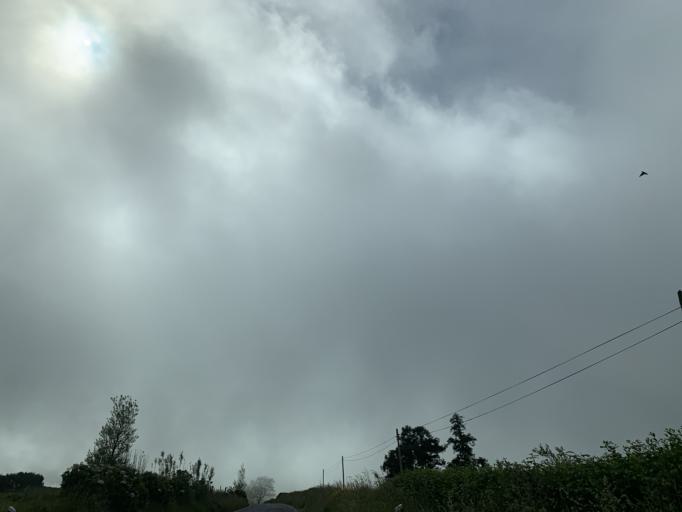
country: PT
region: Azores
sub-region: Ponta Delgada
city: Arrifes
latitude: 37.7751
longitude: -25.7475
